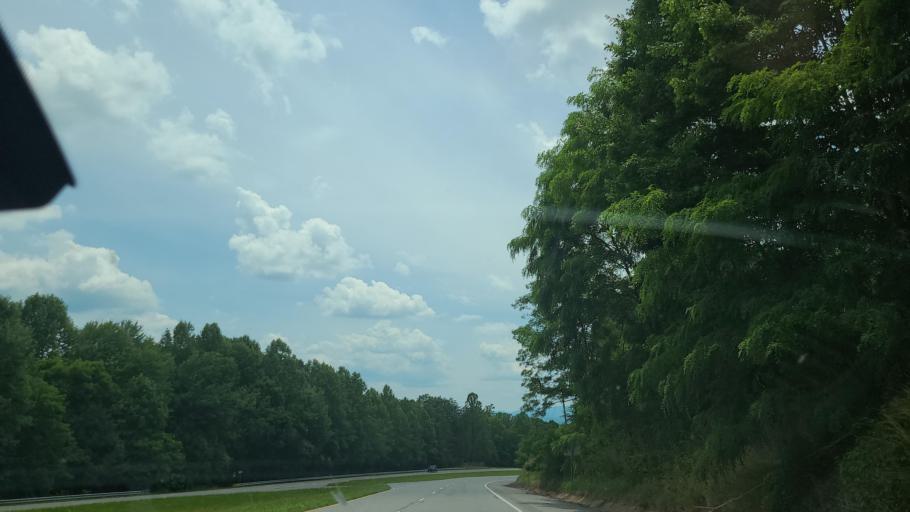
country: US
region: Georgia
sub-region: Fannin County
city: McCaysville
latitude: 35.0157
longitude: -84.2929
